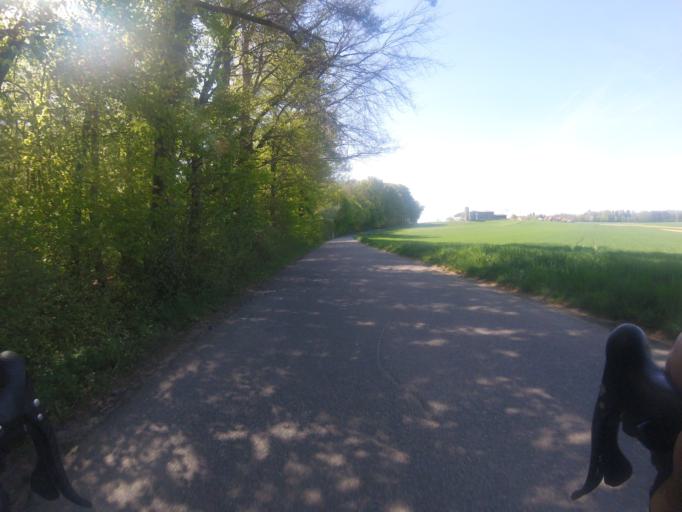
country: CH
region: Bern
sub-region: Bern-Mittelland District
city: Ferenbalm
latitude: 46.9353
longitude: 7.2309
